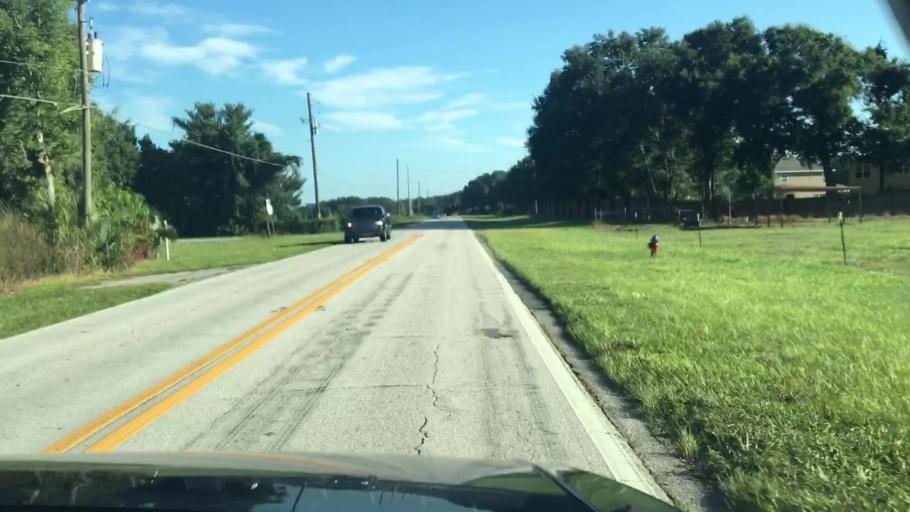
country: US
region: Florida
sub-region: Lake County
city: Eustis
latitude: 28.8651
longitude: -81.6530
